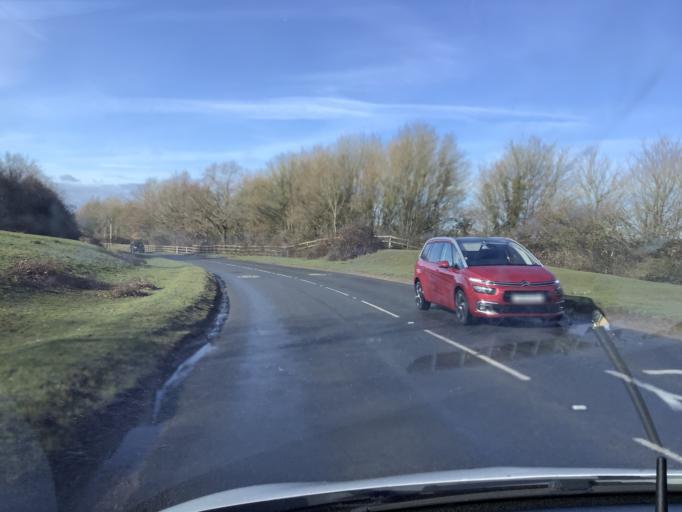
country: GB
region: England
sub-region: Hampshire
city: Hythe
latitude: 50.8157
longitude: -1.4531
